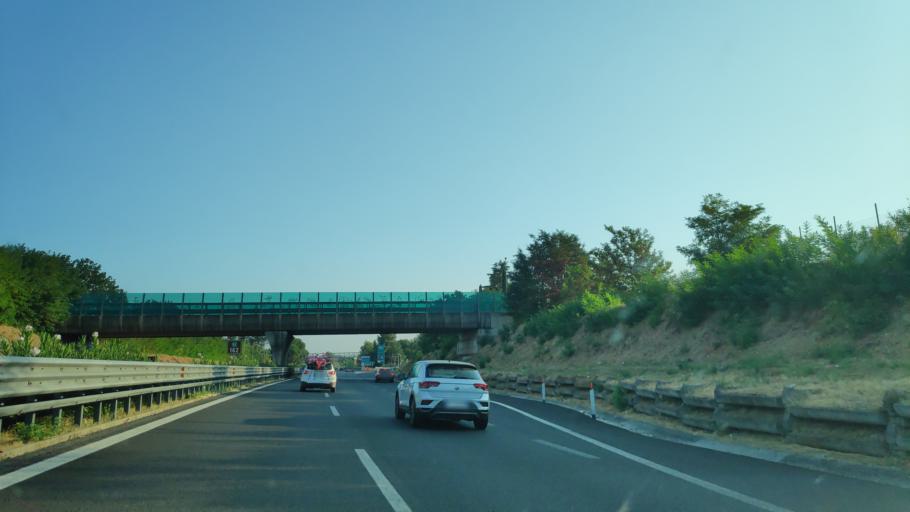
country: IT
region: Calabria
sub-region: Provincia di Cosenza
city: Quattromiglia
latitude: 39.3420
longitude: 16.2346
